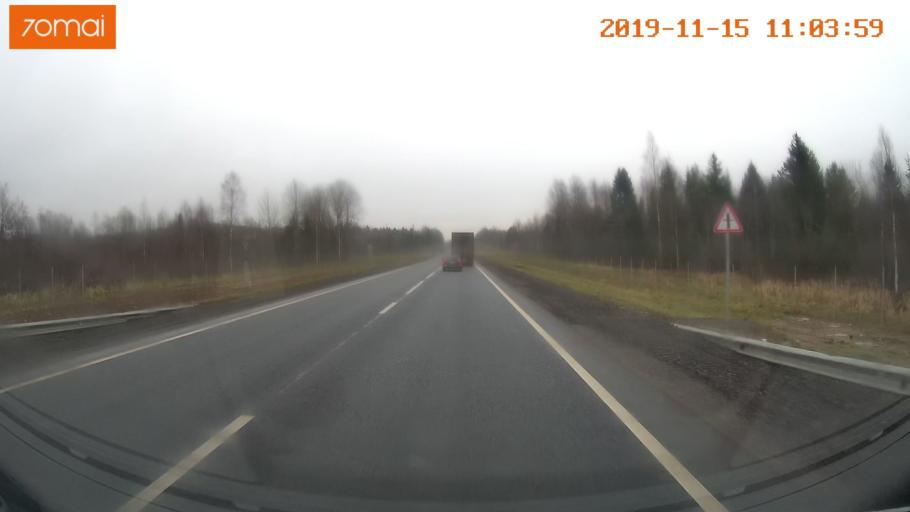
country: RU
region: Vologda
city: Chebsara
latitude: 59.1221
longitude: 38.9739
